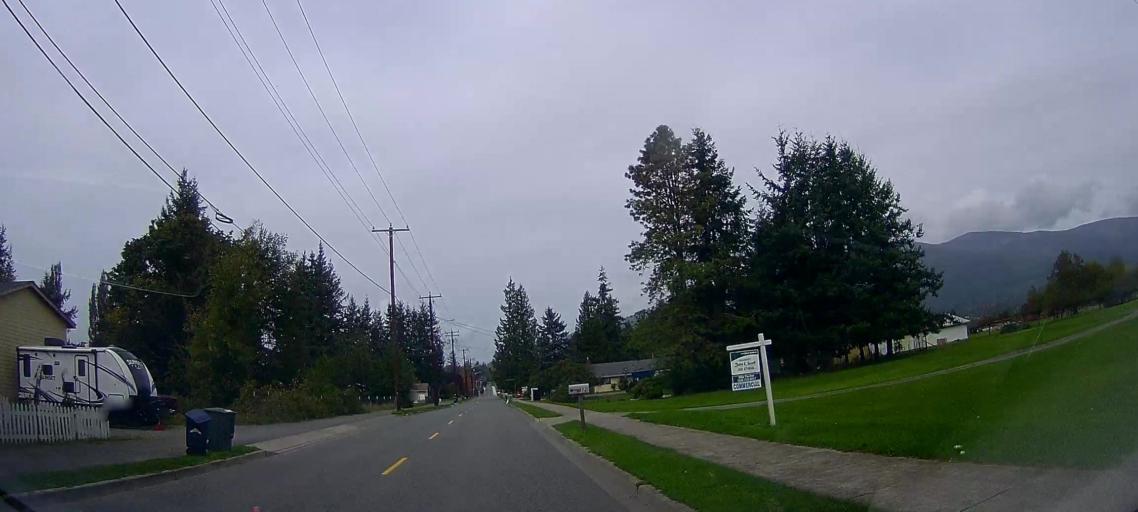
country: US
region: Washington
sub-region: Skagit County
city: Sedro-Woolley
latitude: 48.5188
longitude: -122.2105
